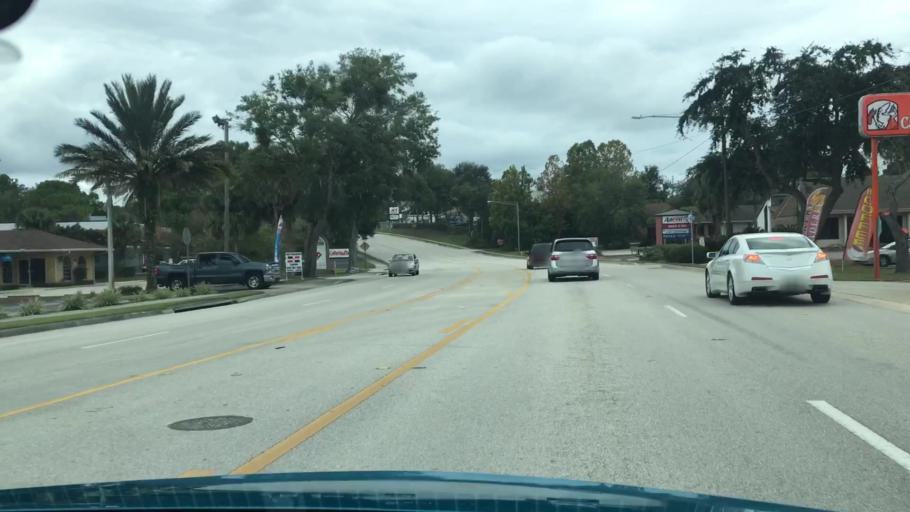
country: US
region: Florida
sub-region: Volusia County
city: Deltona
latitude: 28.9062
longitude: -81.2266
